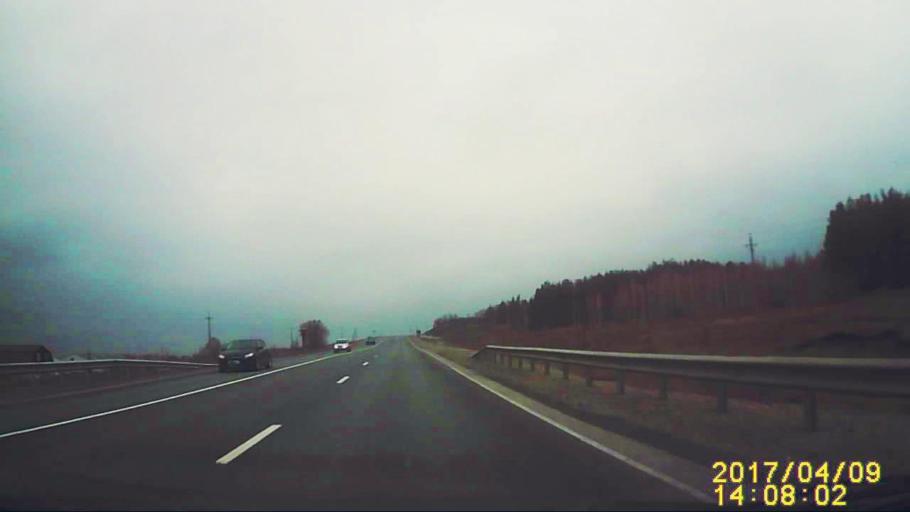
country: RU
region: Ulyanovsk
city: Silikatnyy
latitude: 54.0168
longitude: 48.2165
